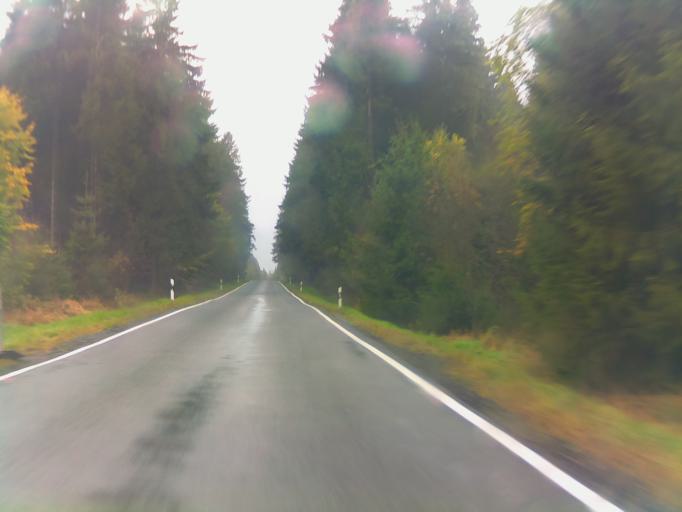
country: DE
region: Thuringia
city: Wurzbach
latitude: 50.4375
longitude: 11.5141
